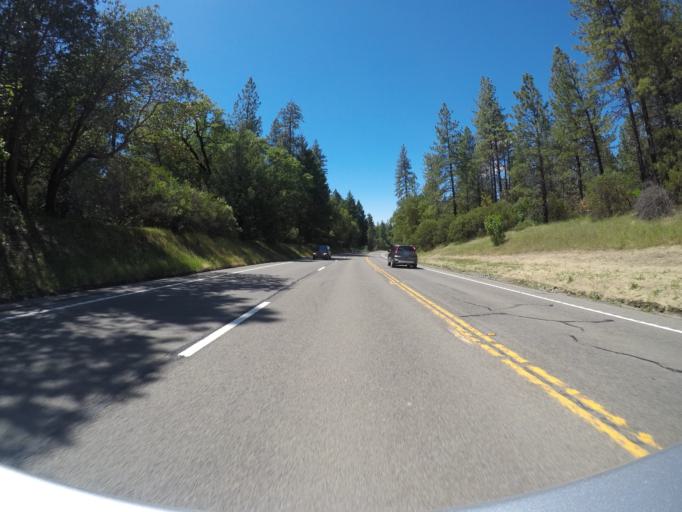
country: US
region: California
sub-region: Mendocino County
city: Laytonville
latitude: 39.7143
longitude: -123.4972
